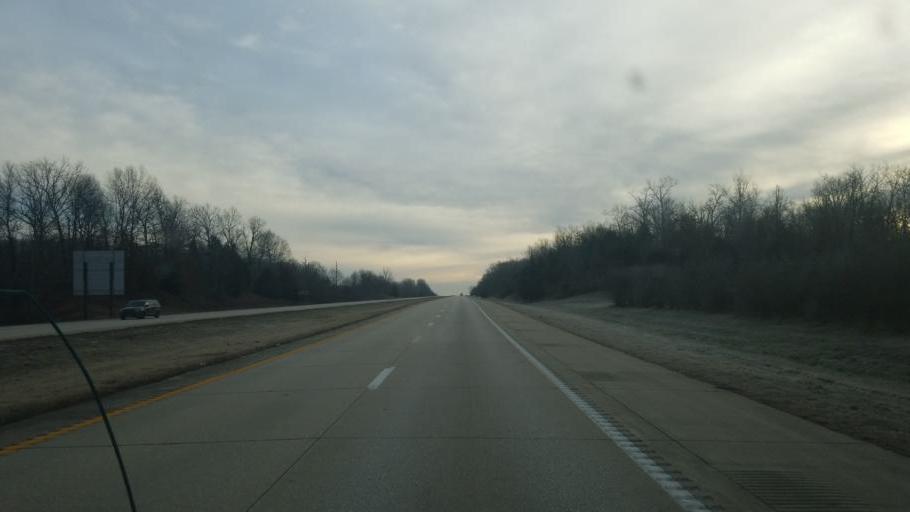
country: US
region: Missouri
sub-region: Butler County
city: Poplar Bluff
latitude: 36.7953
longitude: -90.4200
